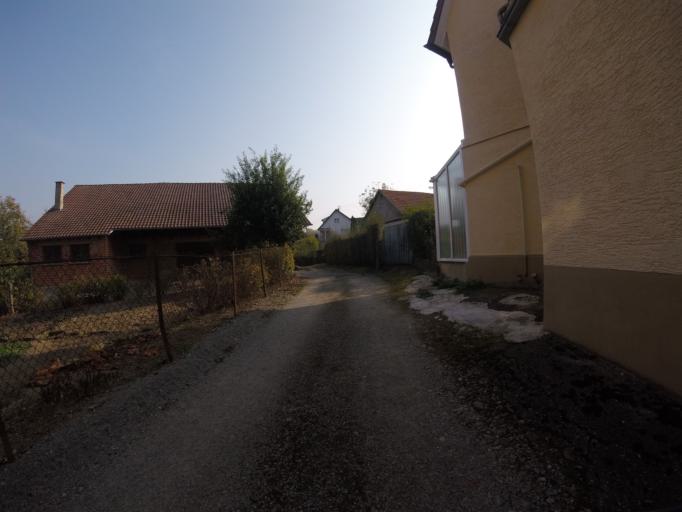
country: DE
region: Baden-Wuerttemberg
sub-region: Regierungsbezirk Stuttgart
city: Mittelschontal
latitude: 48.9484
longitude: 9.3955
